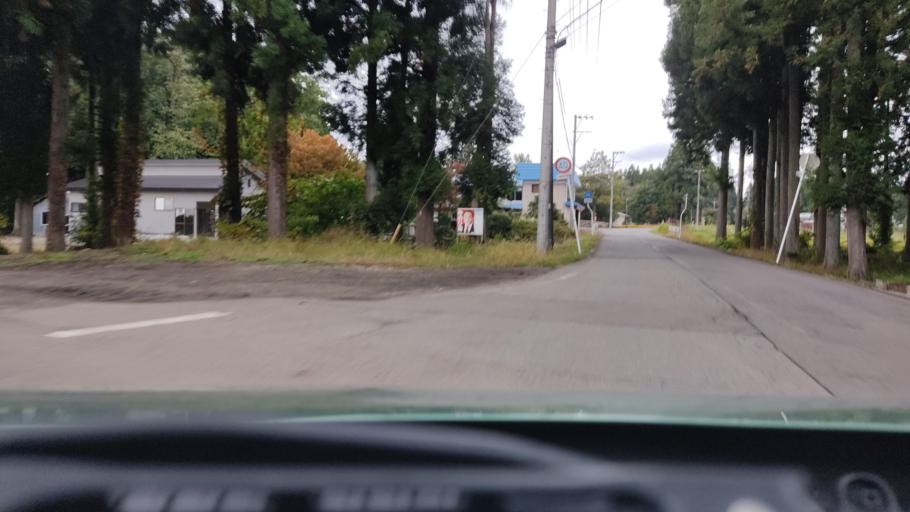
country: JP
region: Akita
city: Kakunodatemachi
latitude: 39.5712
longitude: 140.6129
